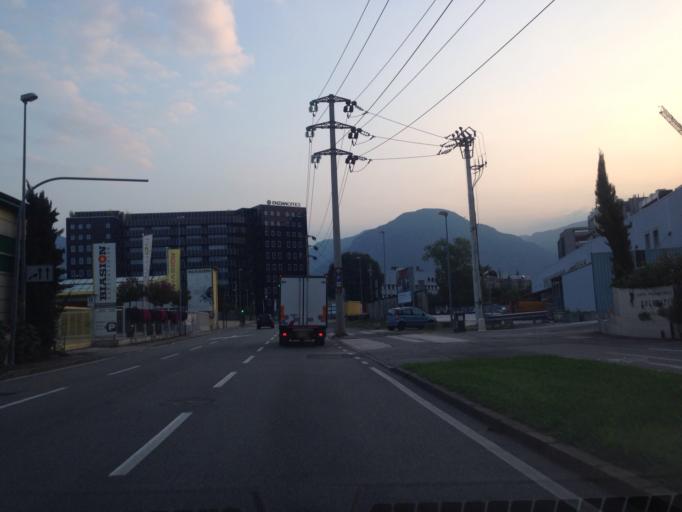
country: IT
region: Trentino-Alto Adige
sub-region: Bolzano
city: Bolzano
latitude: 46.4809
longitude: 11.3268
